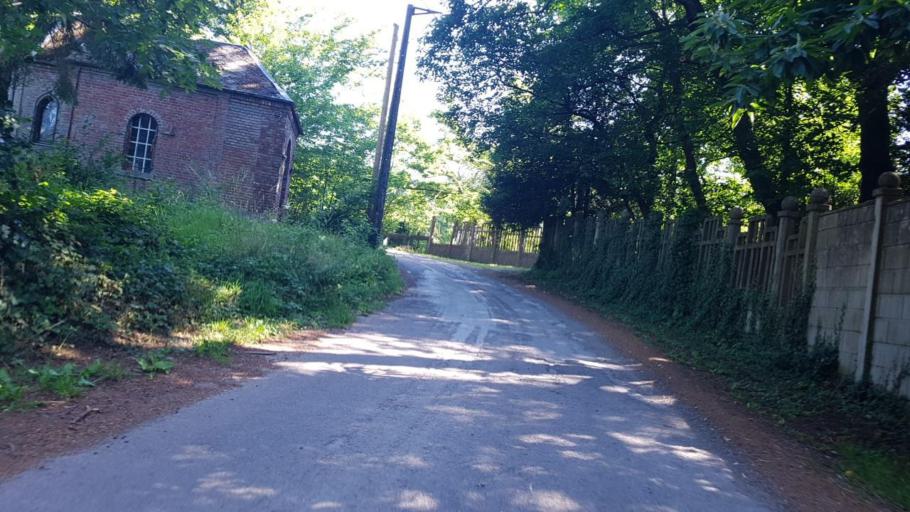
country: FR
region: Nord-Pas-de-Calais
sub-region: Departement du Nord
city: Anor
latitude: 49.9745
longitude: 4.1218
